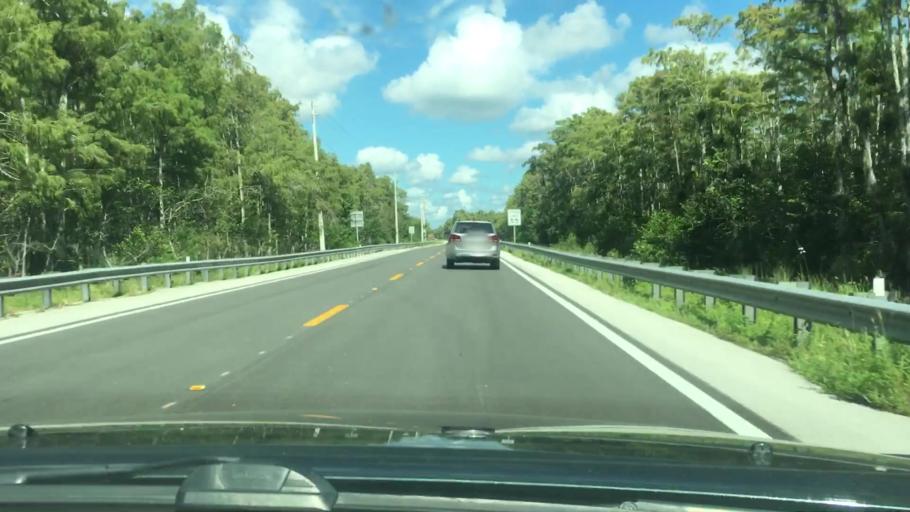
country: US
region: Florida
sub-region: Miami-Dade County
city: Kendall West
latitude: 25.8033
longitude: -80.8708
